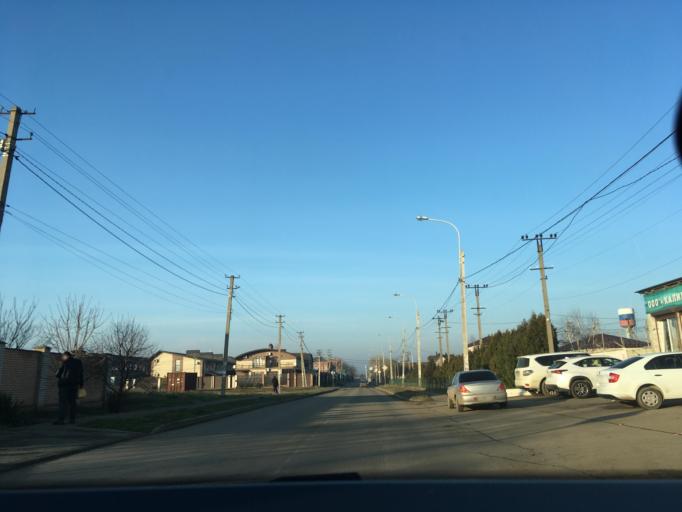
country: RU
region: Krasnodarskiy
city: Krasnodar
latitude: 45.1177
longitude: 39.0145
